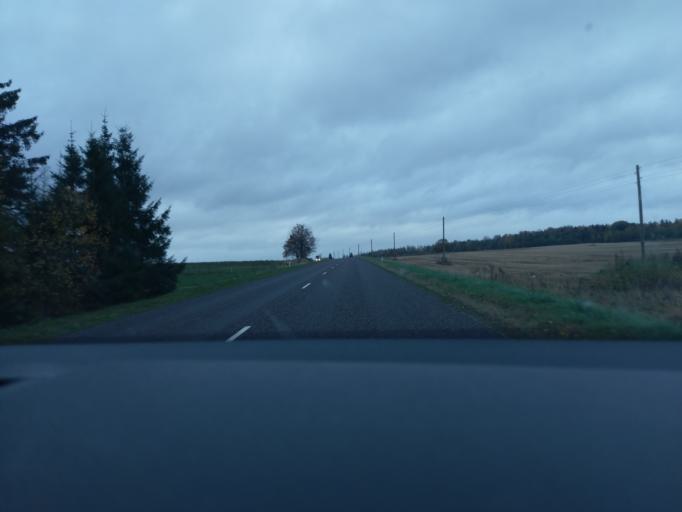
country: LV
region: Kuldigas Rajons
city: Kuldiga
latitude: 57.0105
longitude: 22.1527
